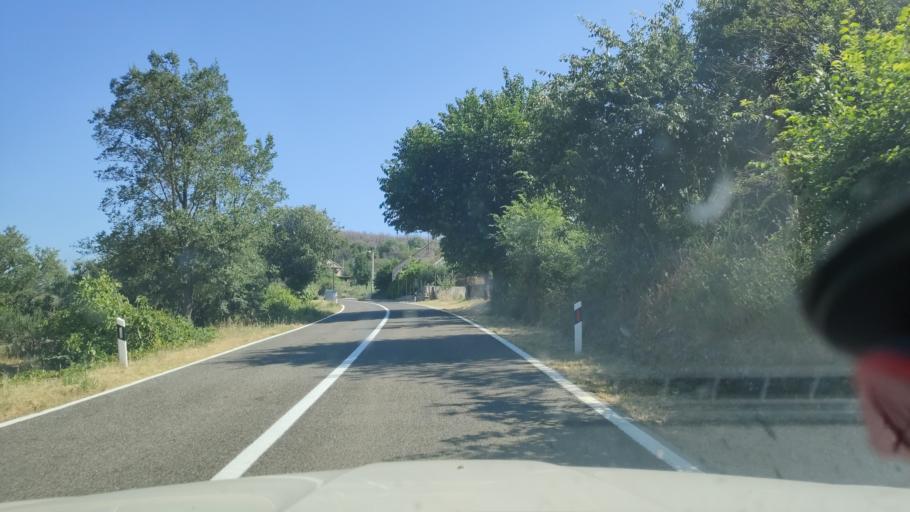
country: HR
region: Sibensko-Kniniska
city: Kistanje
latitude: 43.9353
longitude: 15.8340
